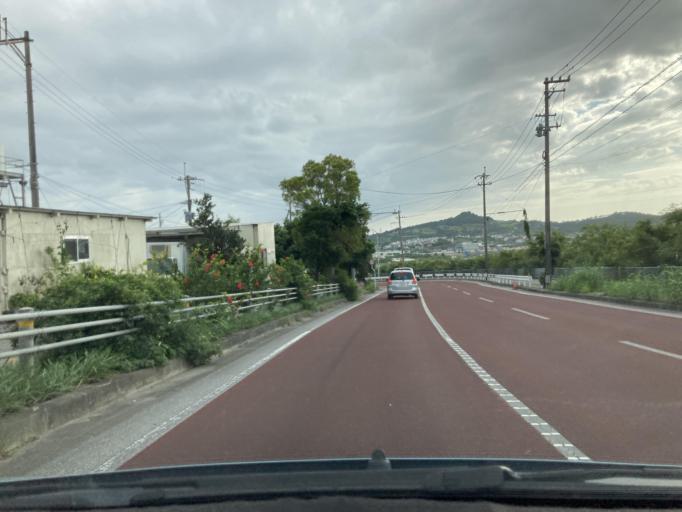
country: JP
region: Okinawa
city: Ginowan
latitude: 26.2327
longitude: 127.7674
